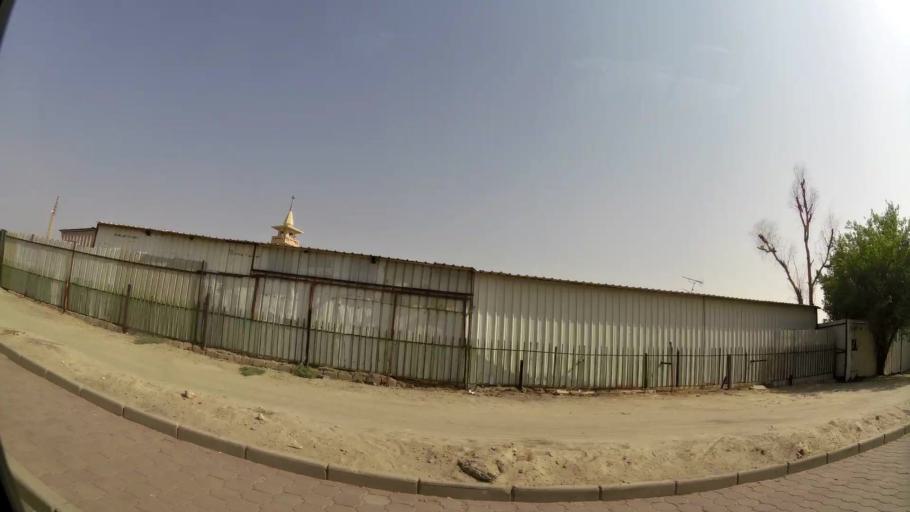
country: KW
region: Muhafazat al Jahra'
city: Al Jahra'
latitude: 29.3331
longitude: 47.6650
